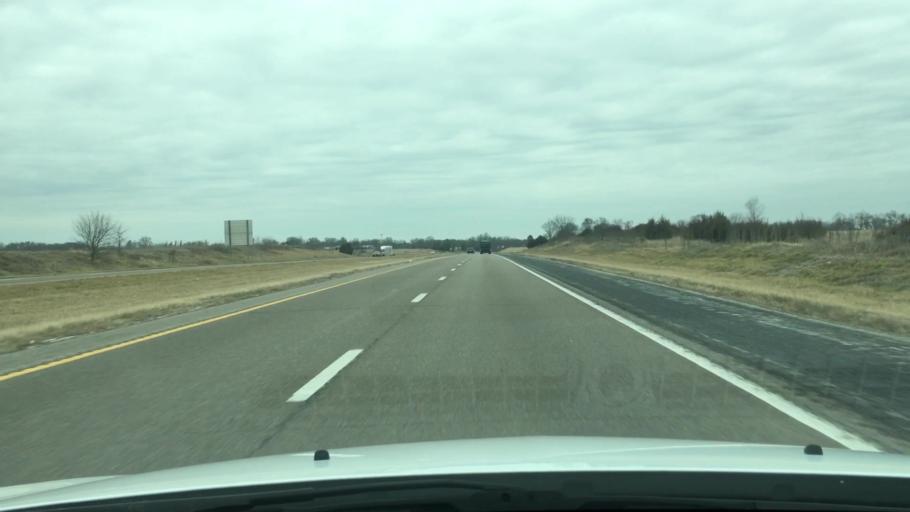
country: US
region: Missouri
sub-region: Audrain County
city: Mexico
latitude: 39.0341
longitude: -91.8885
